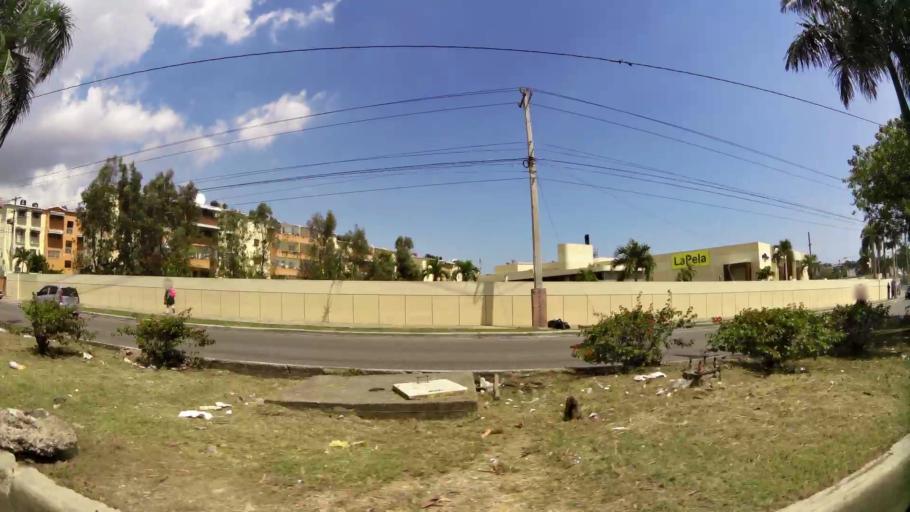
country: DO
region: Santo Domingo
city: Santo Domingo Oeste
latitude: 18.4874
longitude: -70.0004
